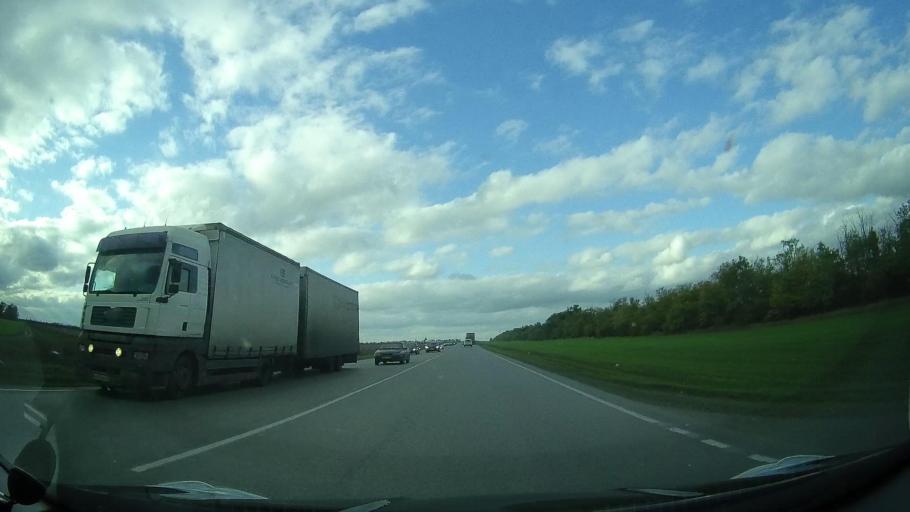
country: RU
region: Rostov
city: Kagal'nitskaya
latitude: 46.9170
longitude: 40.1079
